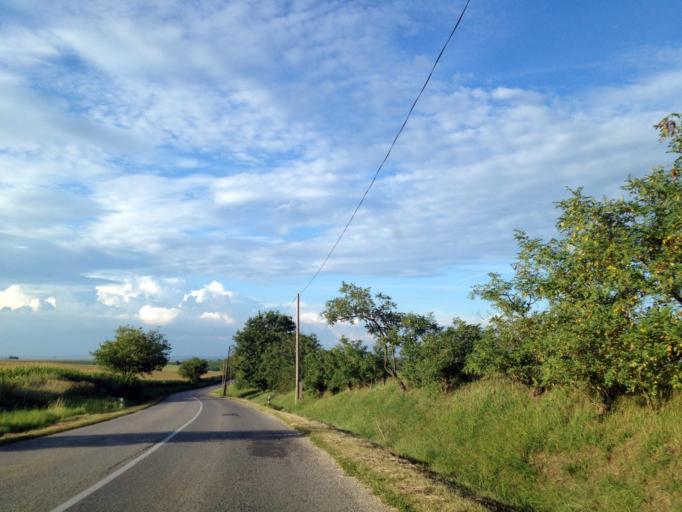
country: SK
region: Nitriansky
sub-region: Okres Komarno
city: Hurbanovo
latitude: 47.8715
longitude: 18.2820
